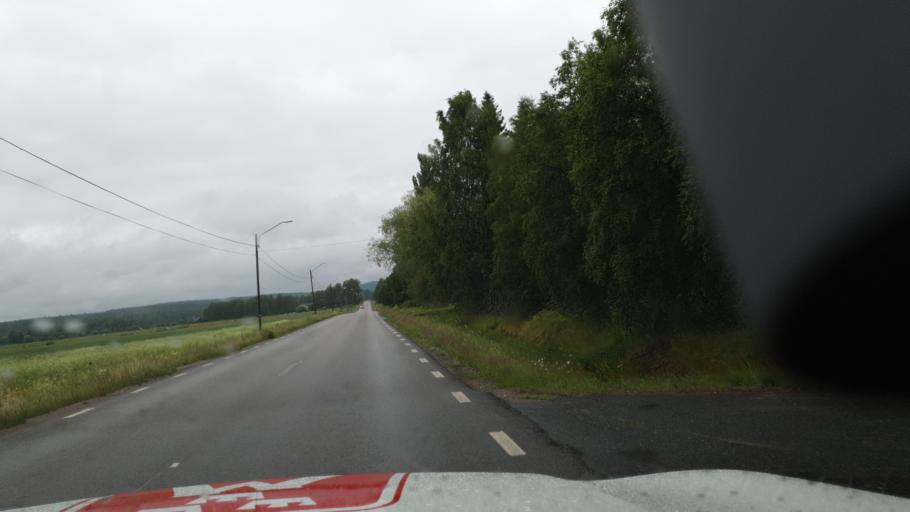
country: SE
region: Vaesterbotten
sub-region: Vannas Kommun
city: Vannasby
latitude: 63.7868
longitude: 19.8622
